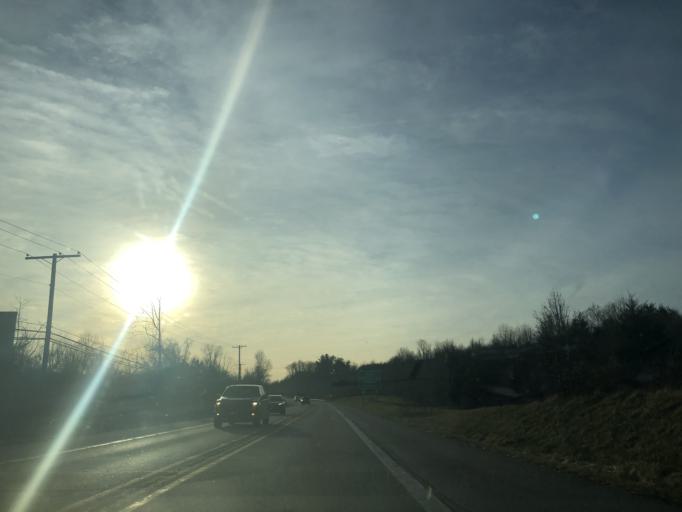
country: US
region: Maryland
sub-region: Carroll County
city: Sykesville
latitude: 39.2815
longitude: -76.9770
